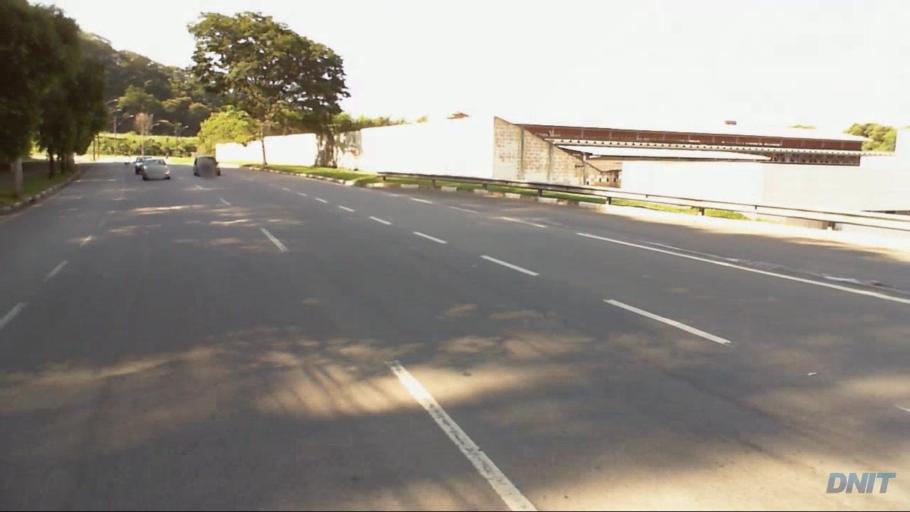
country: BR
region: Minas Gerais
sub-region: Ipatinga
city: Ipatinga
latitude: -19.4934
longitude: -42.5646
